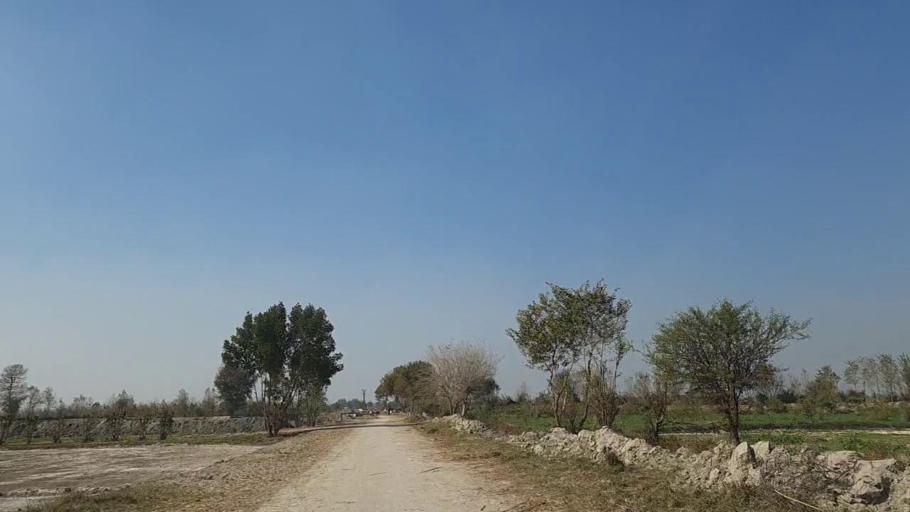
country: PK
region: Sindh
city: Daur
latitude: 26.5001
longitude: 68.3535
